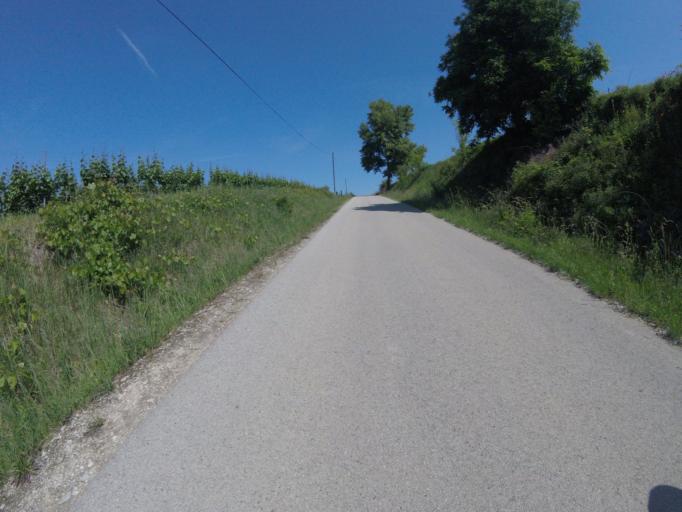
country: HU
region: Zala
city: Zalaszentgrot
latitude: 46.9247
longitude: 17.0541
